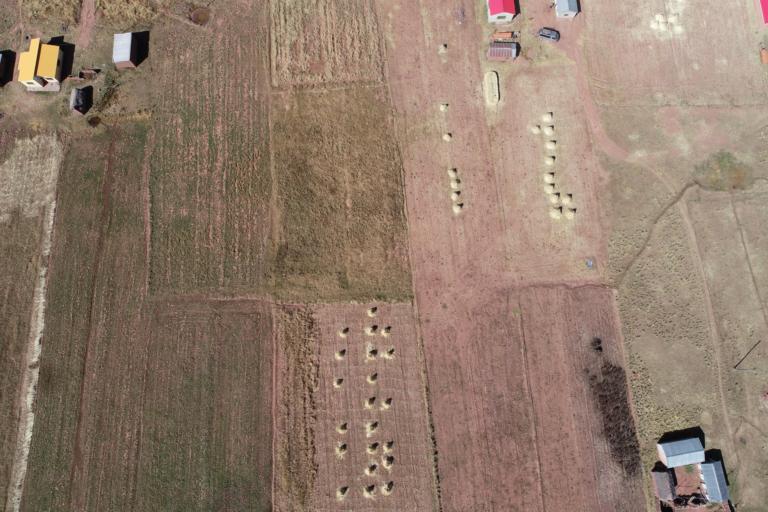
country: BO
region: La Paz
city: Tiahuanaco
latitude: -16.5927
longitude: -68.7561
